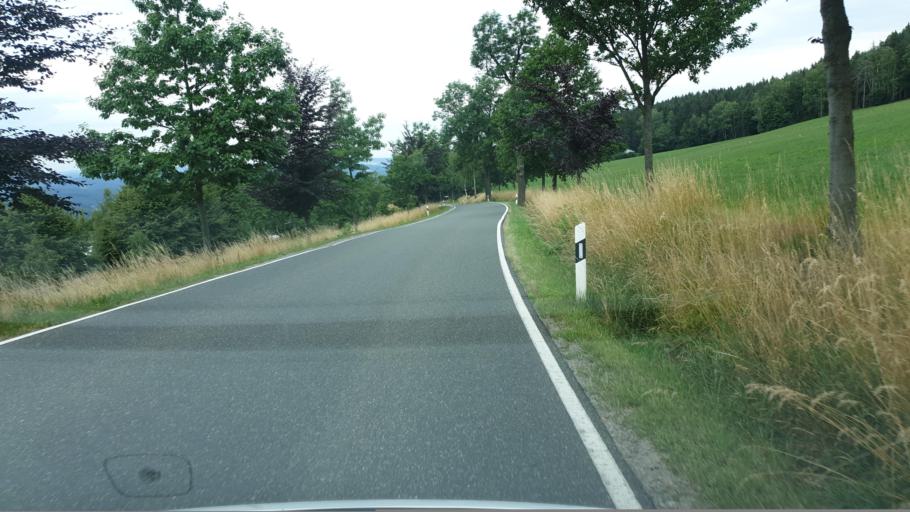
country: DE
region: Saxony
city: Bernsbach
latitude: 50.5826
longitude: 12.7723
